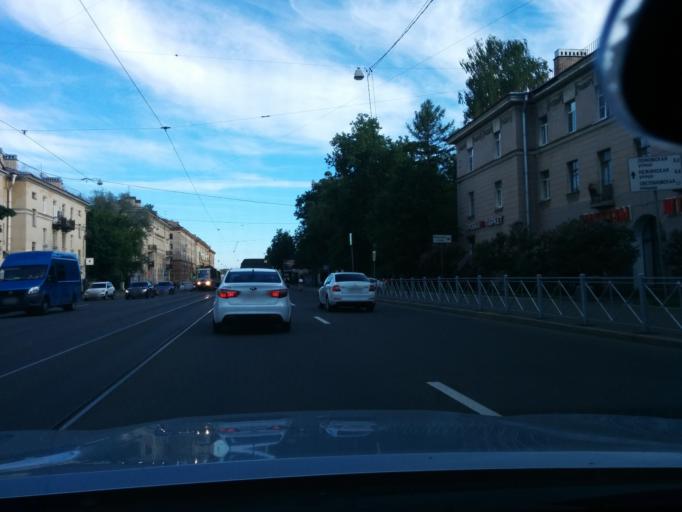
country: RU
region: Leningrad
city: Udel'naya
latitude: 60.0145
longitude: 30.3232
